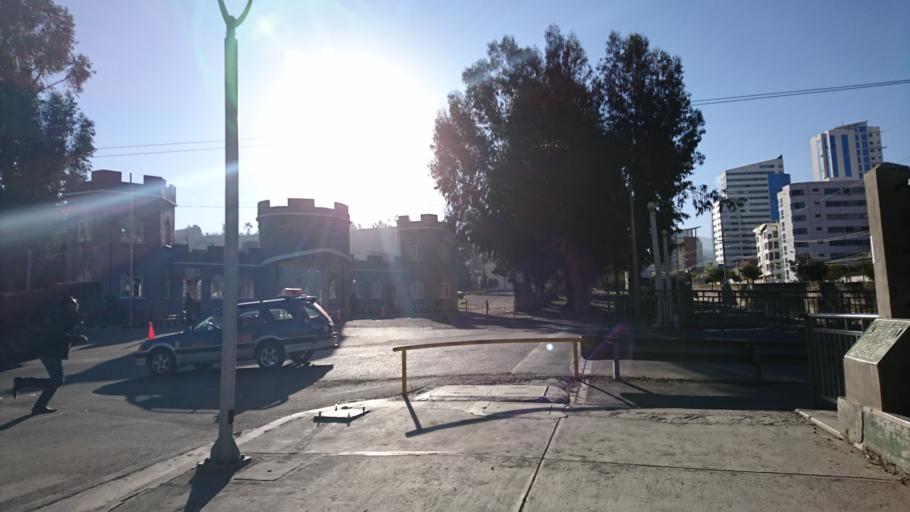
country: BO
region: La Paz
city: La Paz
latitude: -16.5386
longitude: -68.0870
